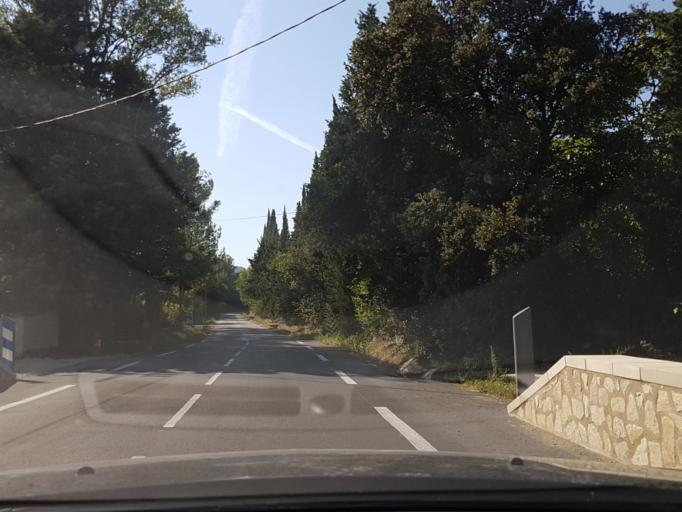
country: FR
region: Provence-Alpes-Cote d'Azur
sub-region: Departement des Bouches-du-Rhone
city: Eygalieres
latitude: 43.7733
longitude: 4.9305
